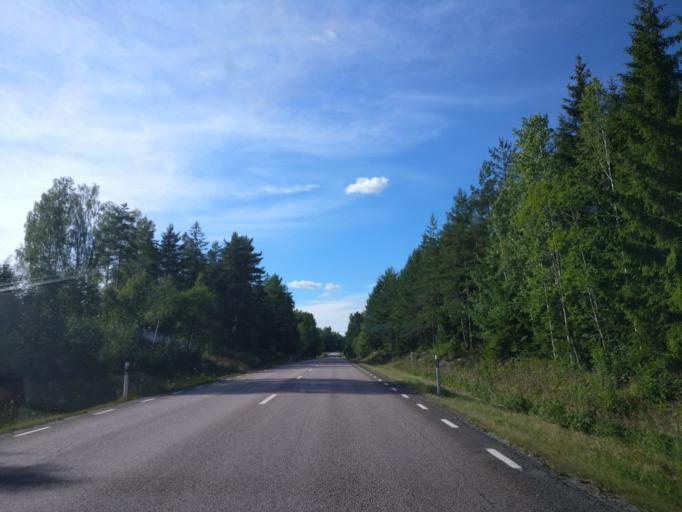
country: SE
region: Vaermland
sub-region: Karlstads Kommun
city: Edsvalla
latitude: 59.5610
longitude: 13.0323
